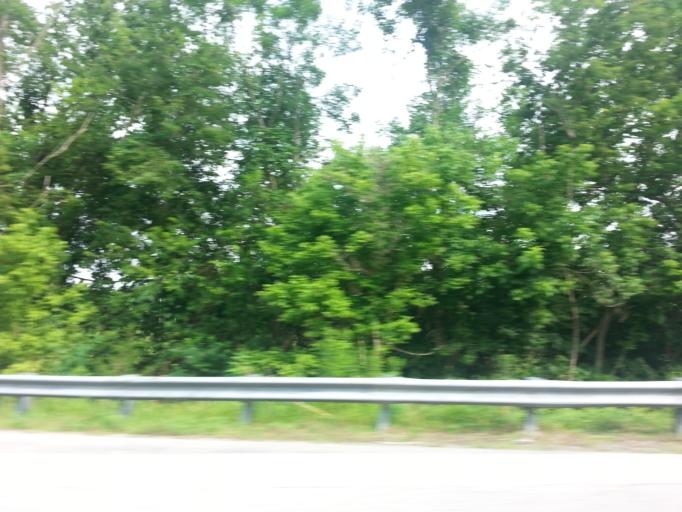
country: US
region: Kentucky
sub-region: Robertson County
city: Mount Olivet
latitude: 38.5193
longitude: -84.1869
